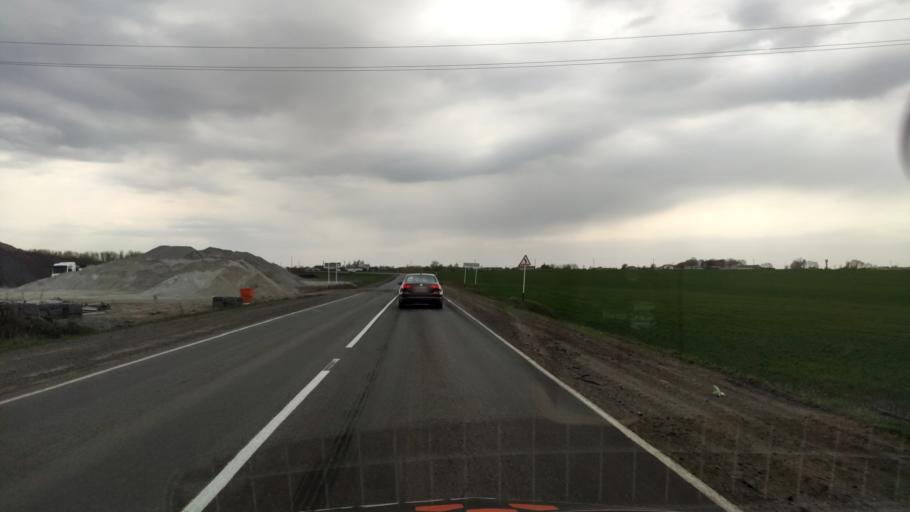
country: RU
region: Kursk
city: Gorshechnoye
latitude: 51.5390
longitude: 38.0236
